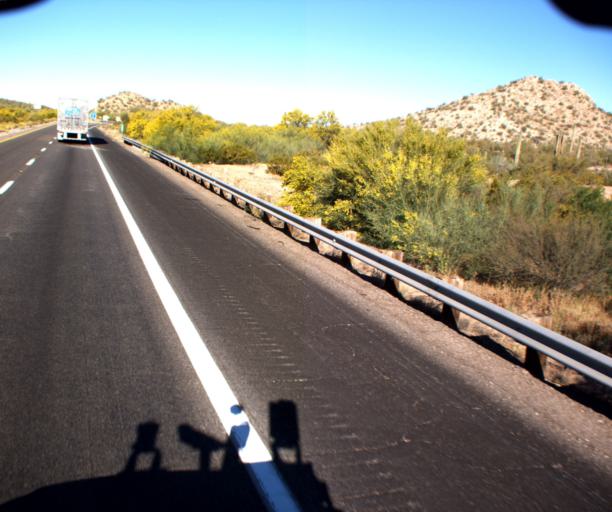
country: US
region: Arizona
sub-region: Pinal County
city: Maricopa
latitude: 32.8350
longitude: -112.1438
